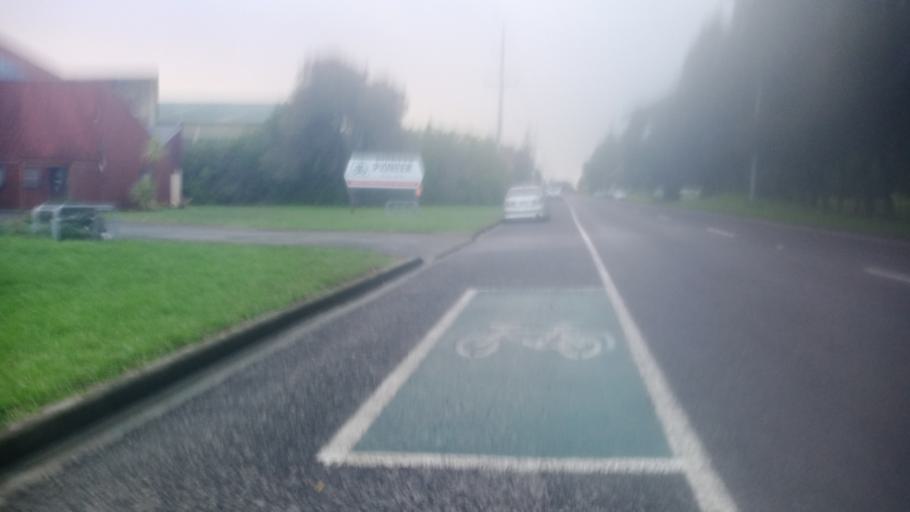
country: NZ
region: Gisborne
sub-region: Gisborne District
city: Gisborne
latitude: -38.6662
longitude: 177.9930
